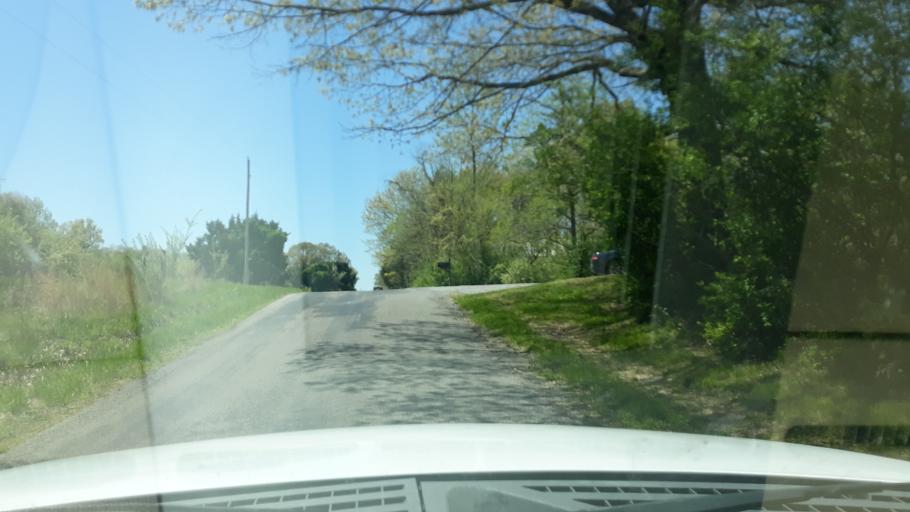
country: US
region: Illinois
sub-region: Saline County
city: Harrisburg
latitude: 37.8597
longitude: -88.6335
